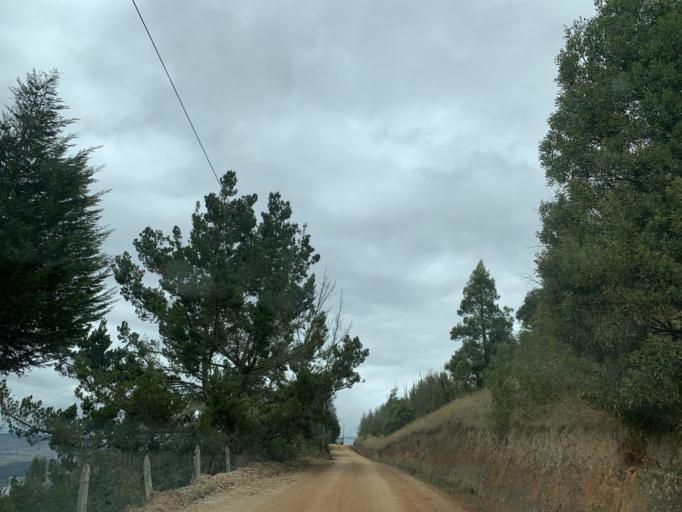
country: CO
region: Boyaca
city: Tunja
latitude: 5.5406
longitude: -73.3203
